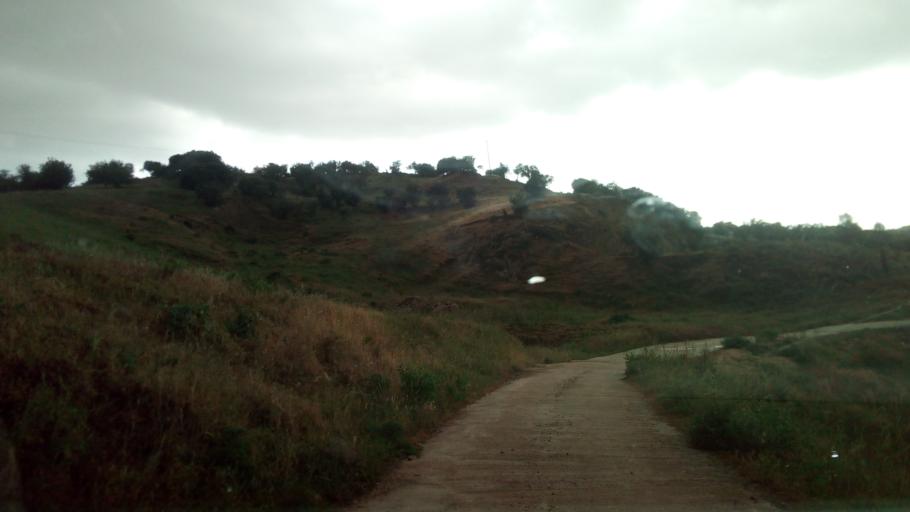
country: CY
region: Pafos
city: Mesogi
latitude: 34.7695
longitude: 32.5657
